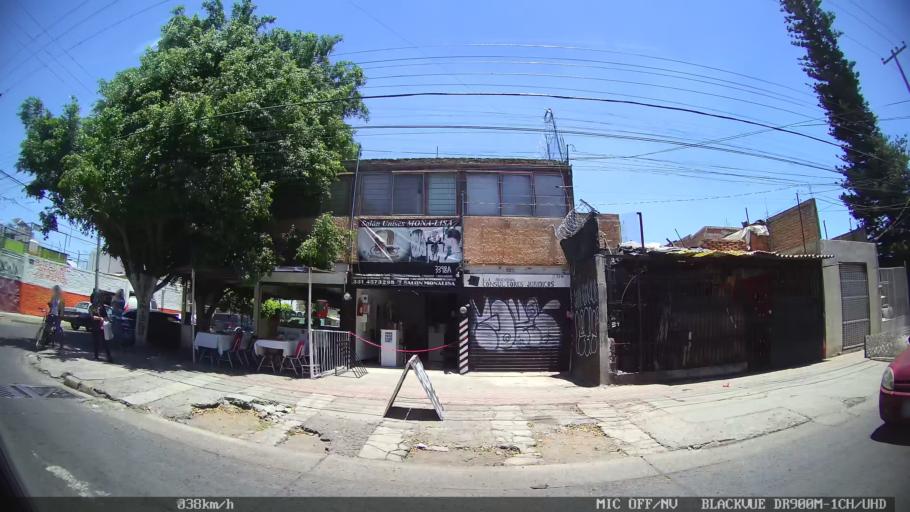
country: MX
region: Jalisco
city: Tlaquepaque
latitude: 20.6615
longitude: -103.2911
